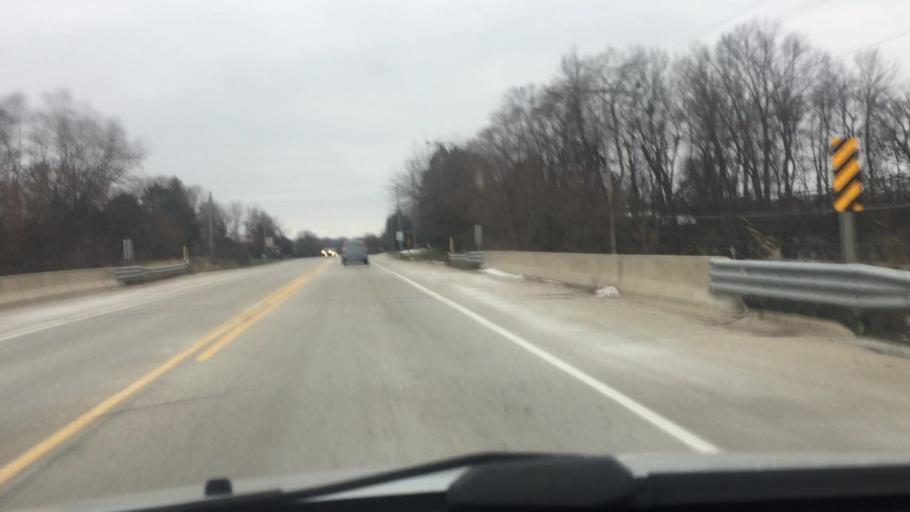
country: US
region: Wisconsin
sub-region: Waukesha County
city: Hartland
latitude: 43.0867
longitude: -88.3632
